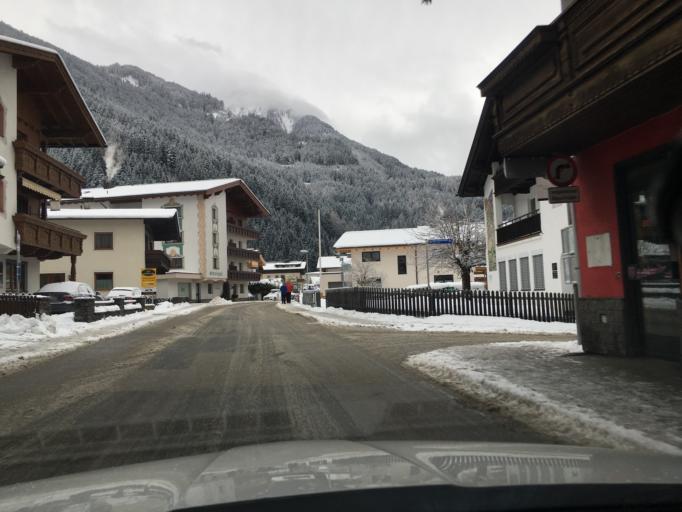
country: AT
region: Tyrol
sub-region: Politischer Bezirk Schwaz
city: Mayrhofen
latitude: 47.1613
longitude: 11.8584
